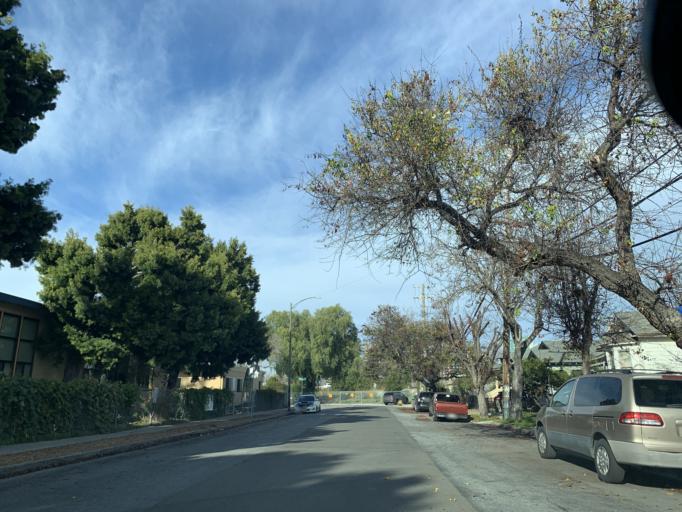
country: US
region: California
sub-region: Santa Clara County
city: San Jose
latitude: 37.3217
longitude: -121.8952
